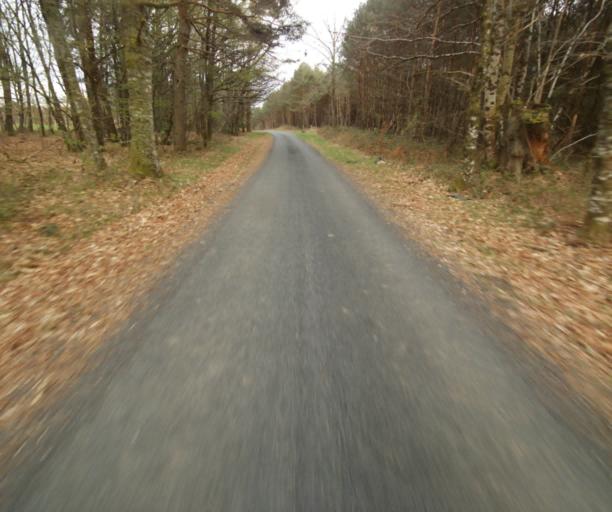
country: FR
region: Limousin
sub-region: Departement de la Correze
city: Saint-Privat
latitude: 45.1994
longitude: 1.9997
